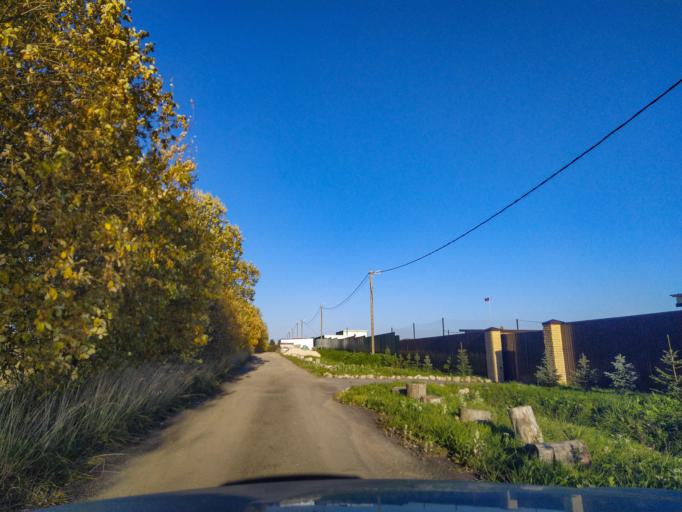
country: RU
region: Leningrad
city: Siverskiy
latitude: 59.3214
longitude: 30.0439
